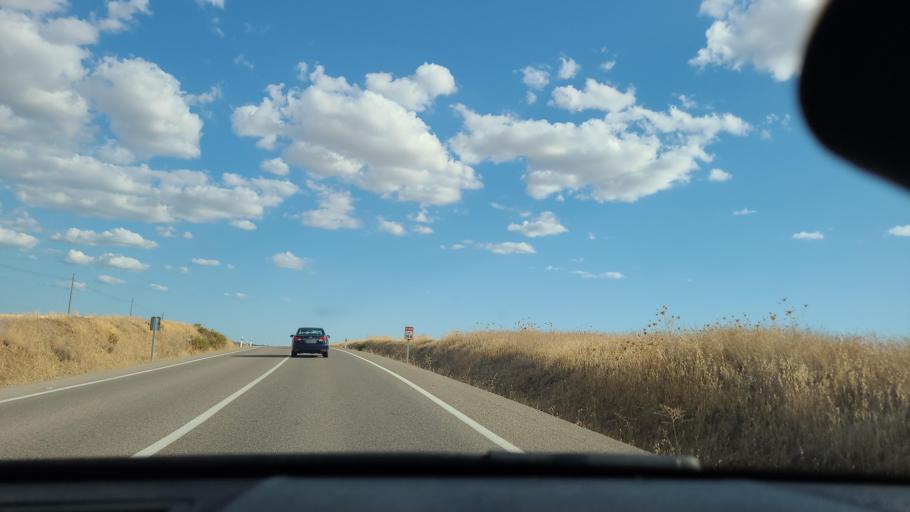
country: ES
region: Extremadura
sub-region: Provincia de Badajoz
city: Granja de Torrehermosa
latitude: 38.2784
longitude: -5.5173
